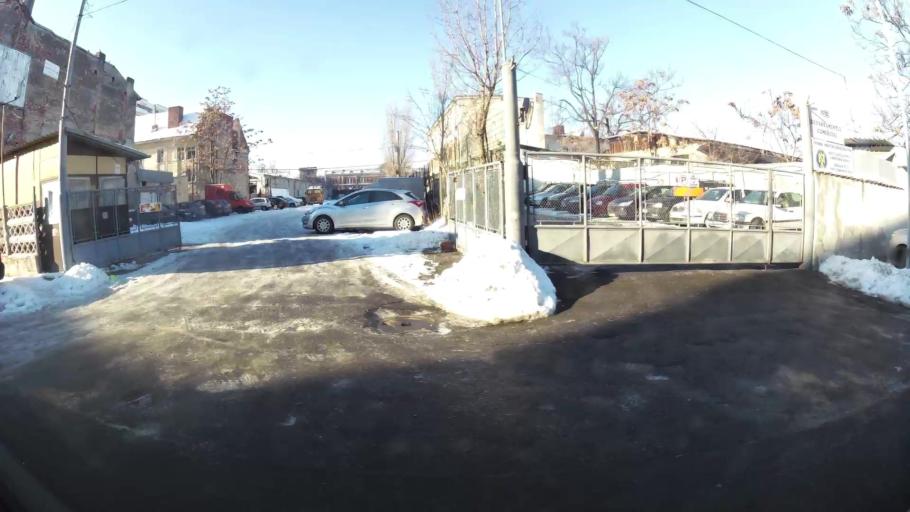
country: RO
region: Bucuresti
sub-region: Municipiul Bucuresti
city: Bucuresti
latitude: 44.4169
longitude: 26.1007
